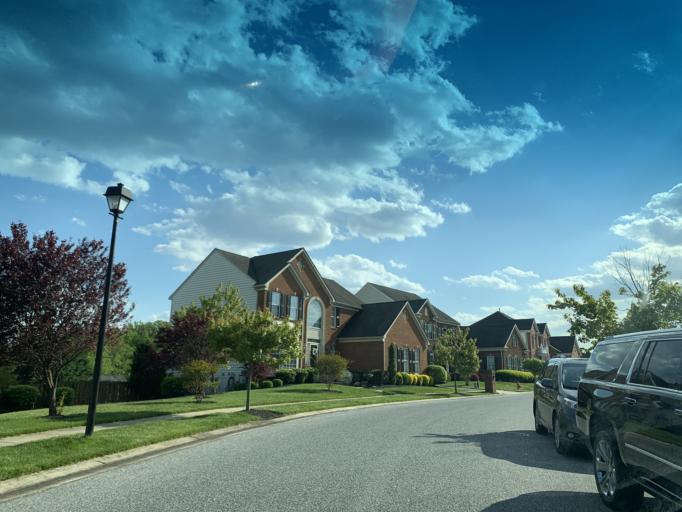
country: US
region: Maryland
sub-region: Baltimore County
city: White Marsh
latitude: 39.4046
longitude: -76.4323
